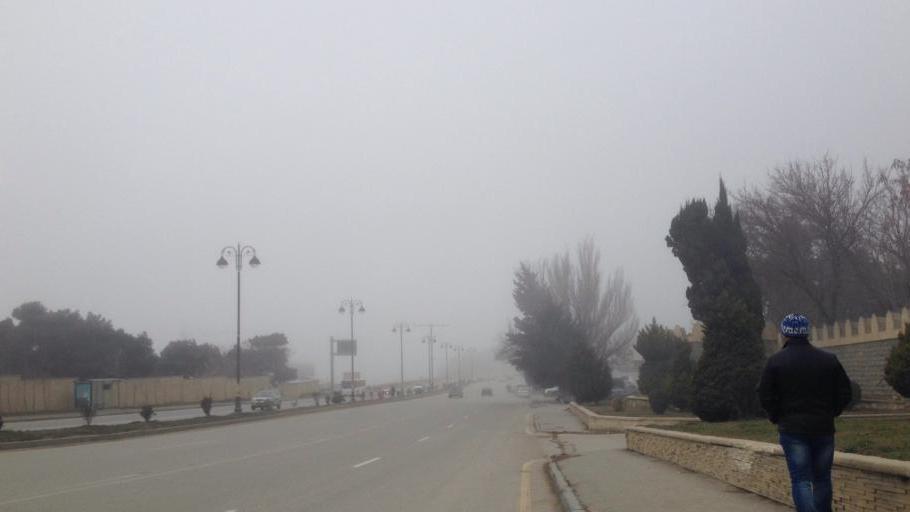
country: AZ
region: Baki
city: Qaracuxur
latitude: 40.3532
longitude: 49.9575
